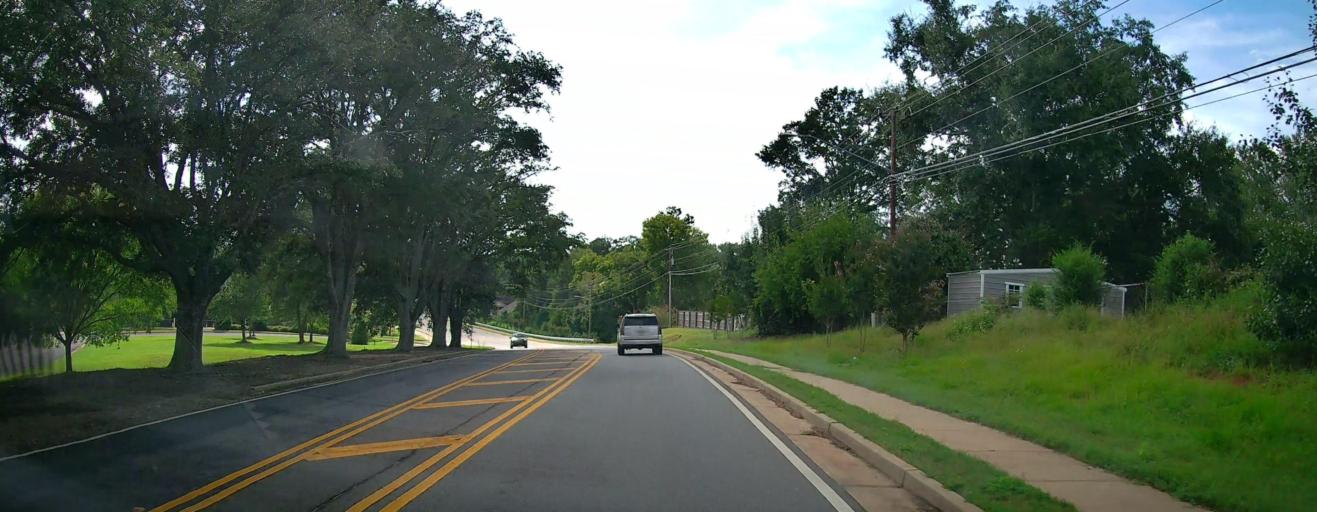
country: US
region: Alabama
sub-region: Russell County
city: Phenix City
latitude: 32.5295
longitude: -84.9884
